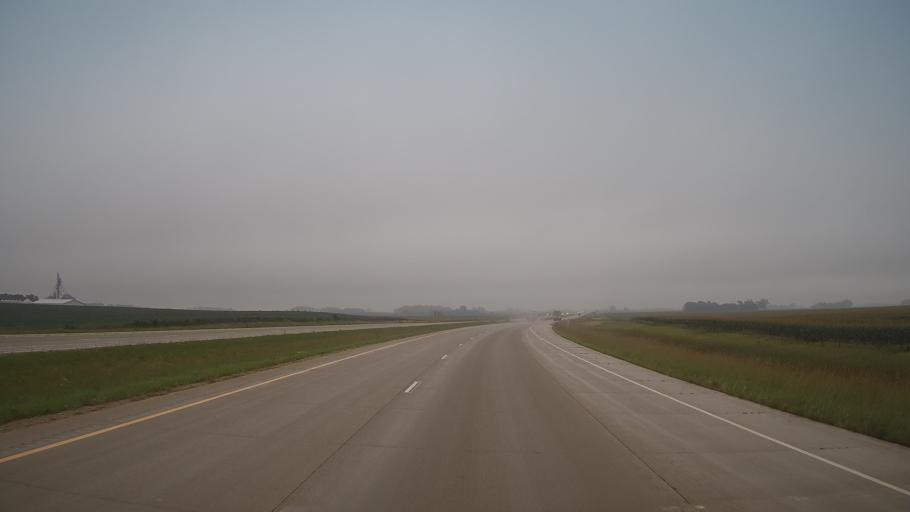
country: US
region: Minnesota
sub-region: Faribault County
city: Wells
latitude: 43.6588
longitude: -93.7223
